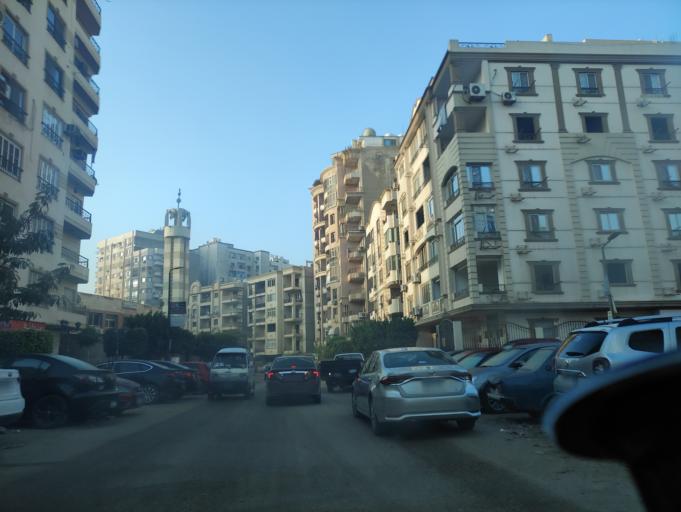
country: EG
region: Muhafazat al Qahirah
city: Cairo
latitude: 30.0497
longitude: 31.3695
